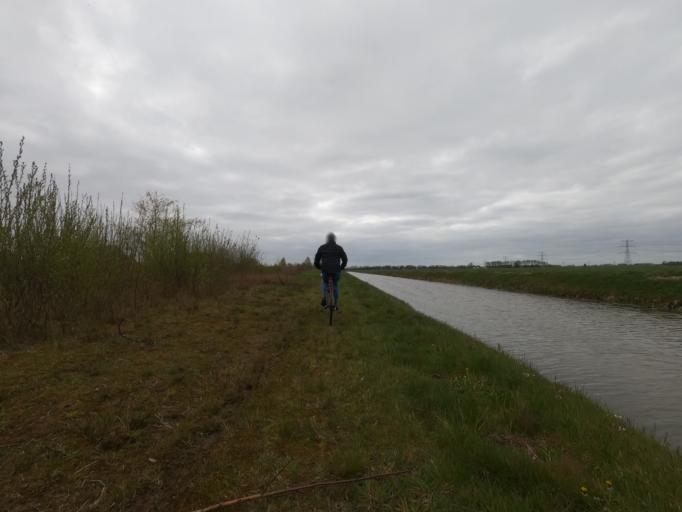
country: NL
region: Drenthe
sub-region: Gemeente Coevorden
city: Sleen
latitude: 52.7561
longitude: 6.8489
